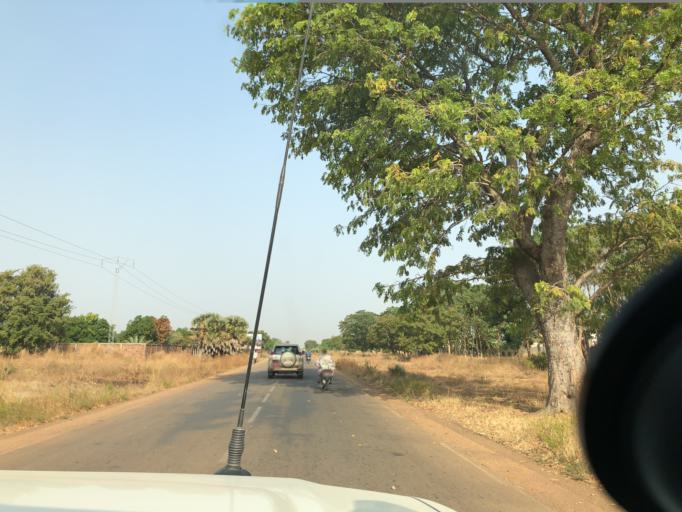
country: TD
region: Logone Occidental
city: Moundou
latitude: 8.5833
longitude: 16.0268
